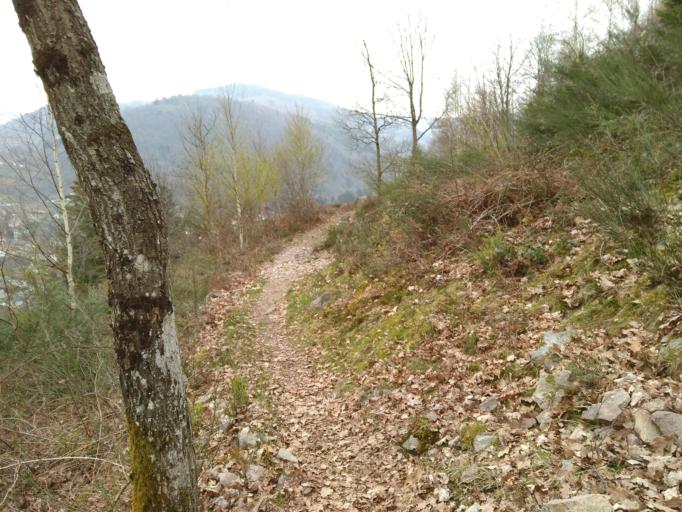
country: FR
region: Lorraine
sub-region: Departement des Vosges
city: Cornimont
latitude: 47.9577
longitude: 6.8359
